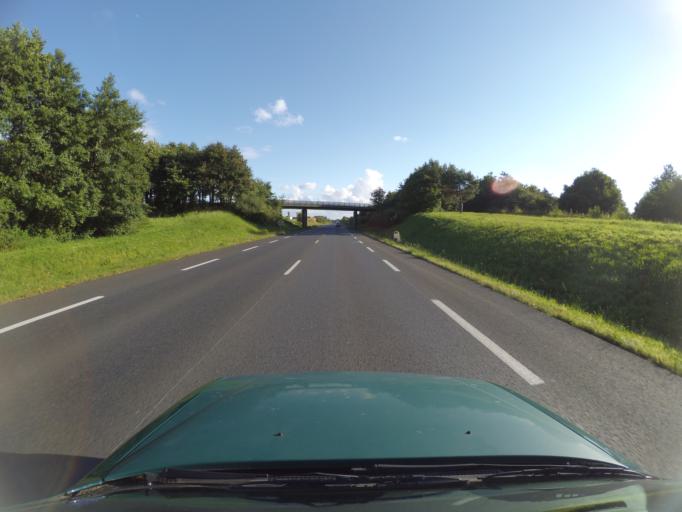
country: FR
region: Pays de la Loire
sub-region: Departement de la Vendee
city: Saint-Hilaire-de-Loulay
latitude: 47.0053
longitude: -1.3422
